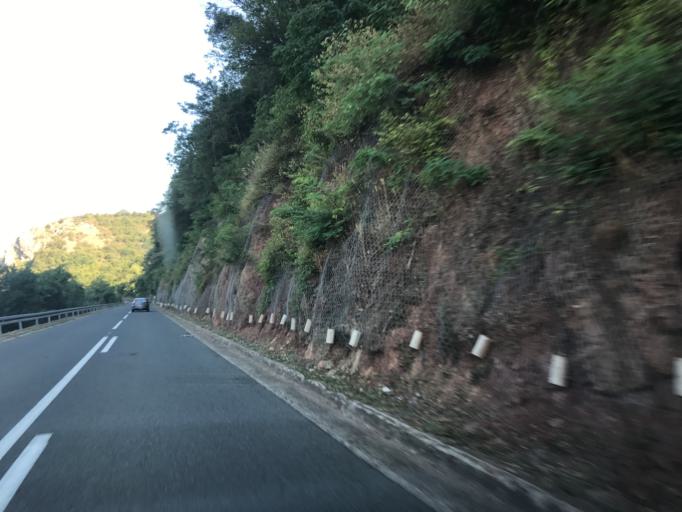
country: RO
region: Mehedinti
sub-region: Comuna Svinita
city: Svinita
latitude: 44.4857
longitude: 22.0812
